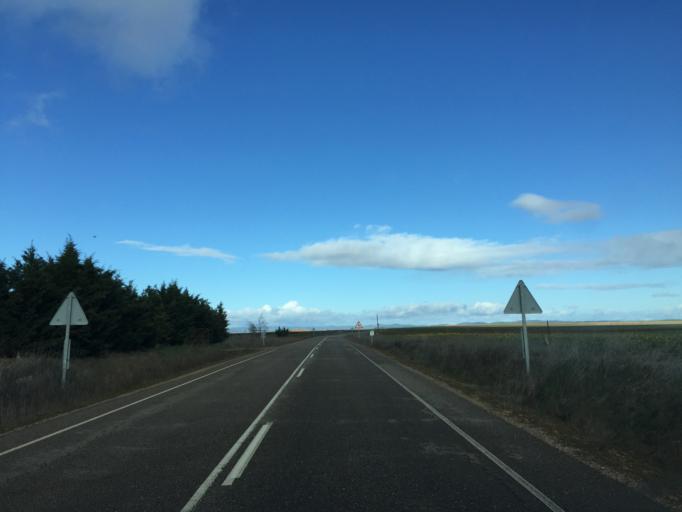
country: ES
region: Castille and Leon
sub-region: Provincia de Zamora
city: Manganeses de la Lampreana
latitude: 41.7565
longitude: -5.7217
